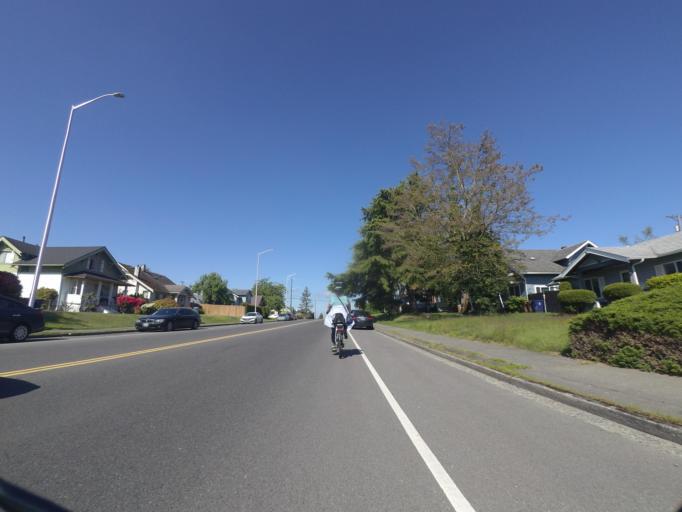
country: US
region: Washington
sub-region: Pierce County
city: Tacoma
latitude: 47.2065
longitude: -122.4385
